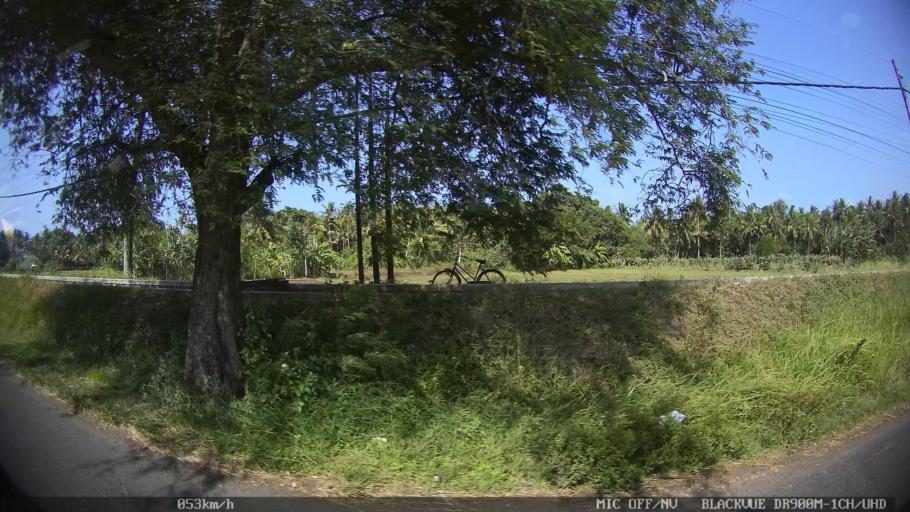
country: ID
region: Daerah Istimewa Yogyakarta
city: Srandakan
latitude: -7.9227
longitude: 110.1856
